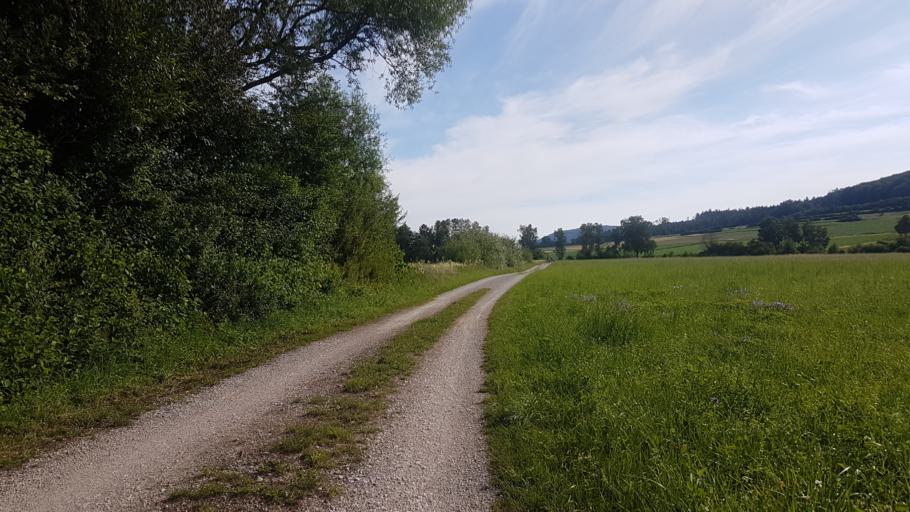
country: DE
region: Bavaria
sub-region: Regierungsbezirk Mittelfranken
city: Treuchtlingen
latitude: 48.9704
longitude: 10.9135
